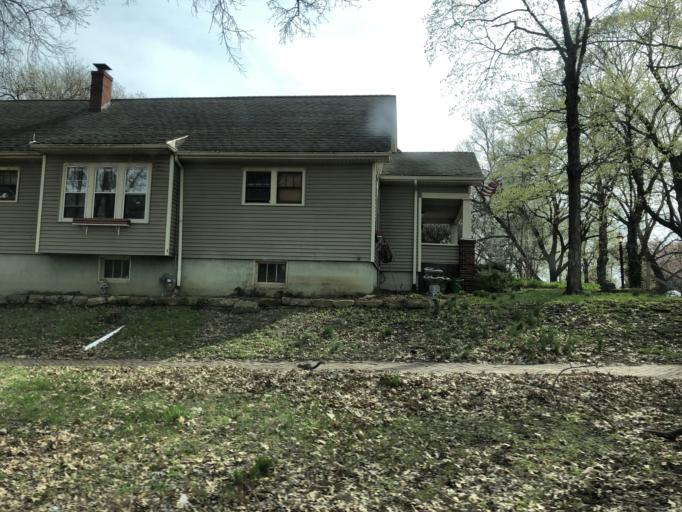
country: US
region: Kansas
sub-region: Leavenworth County
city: Leavenworth
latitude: 39.3125
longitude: -94.9173
